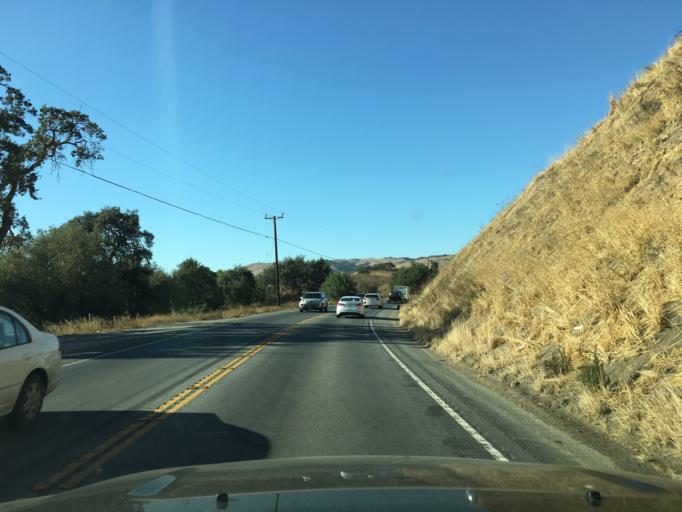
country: US
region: California
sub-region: San Benito County
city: Hollister
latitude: 36.9782
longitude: -121.4374
